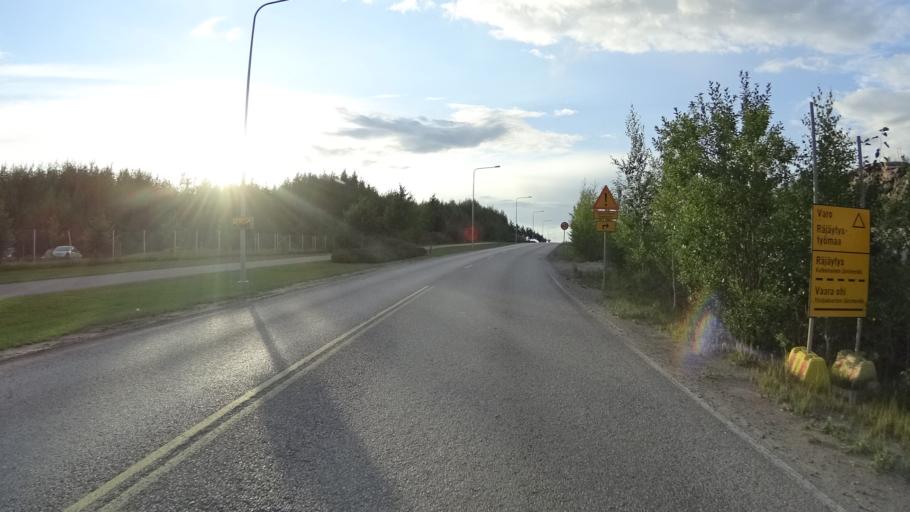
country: FI
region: Uusimaa
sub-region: Helsinki
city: Teekkarikylae
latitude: 60.3041
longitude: 24.9060
